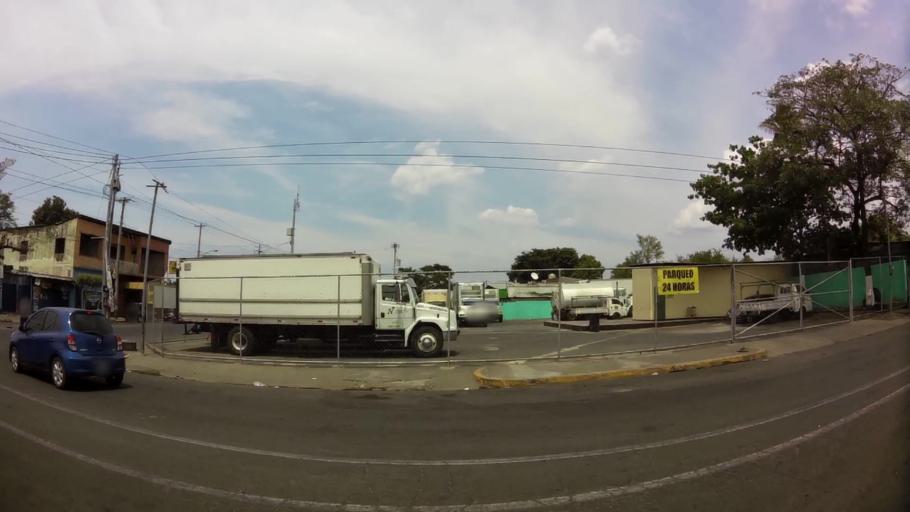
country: NI
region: Managua
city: Managua
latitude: 12.1573
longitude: -86.2875
